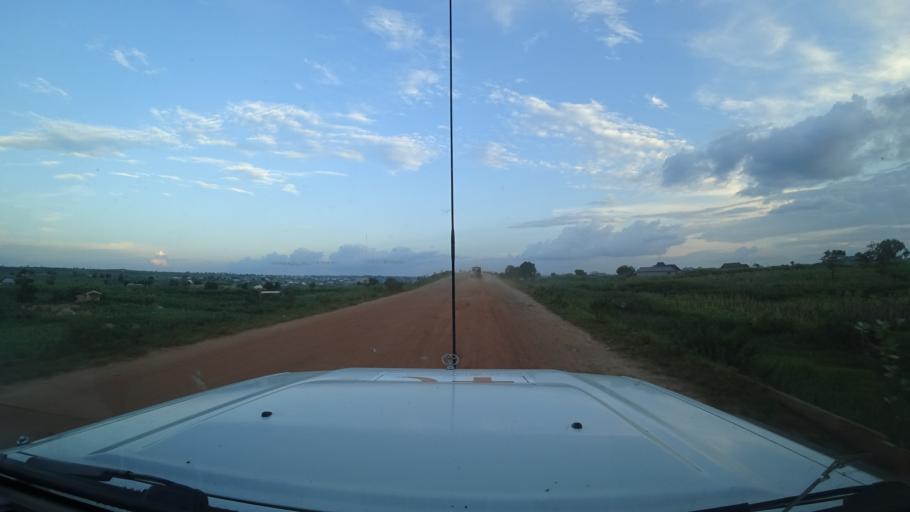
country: NG
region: Niger
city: Minna
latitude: 9.6534
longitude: 6.5766
